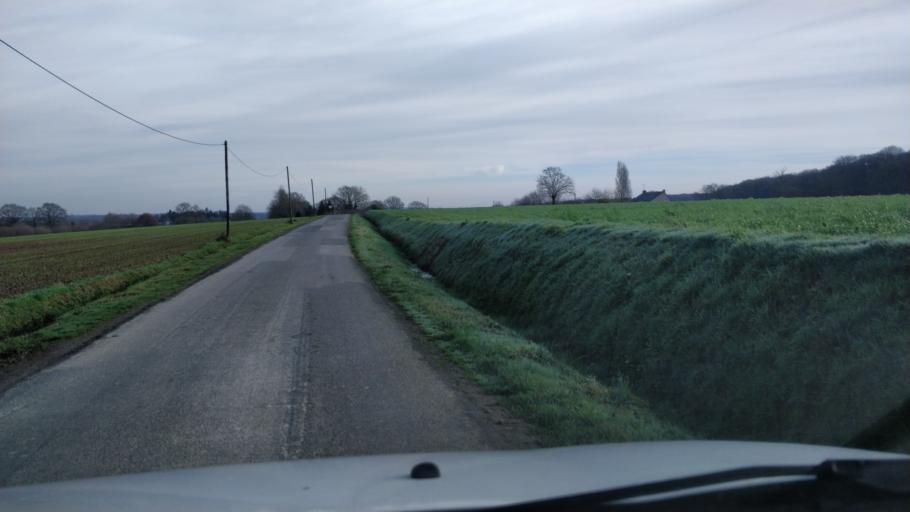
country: FR
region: Brittany
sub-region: Departement d'Ille-et-Vilaine
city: Etrelles
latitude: 48.0236
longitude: -1.1867
